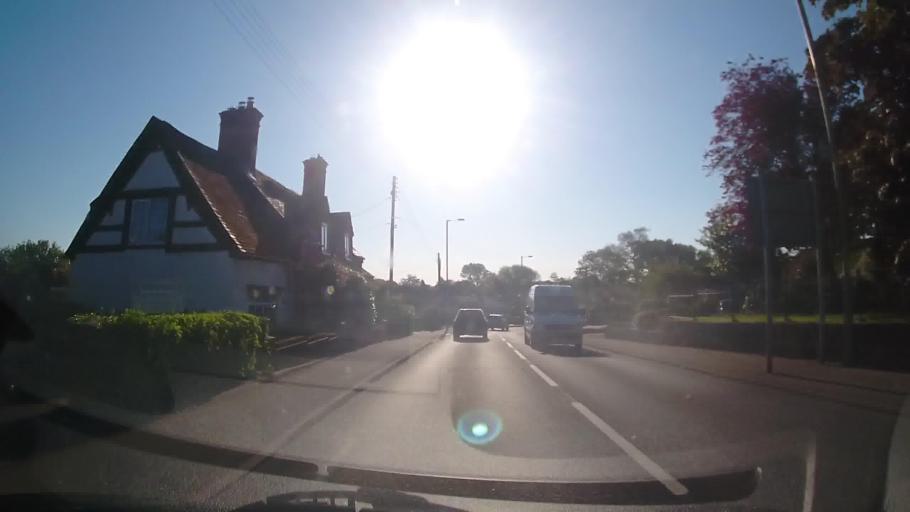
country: GB
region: England
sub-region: Shropshire
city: Shawbury
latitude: 52.7878
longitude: -2.6548
